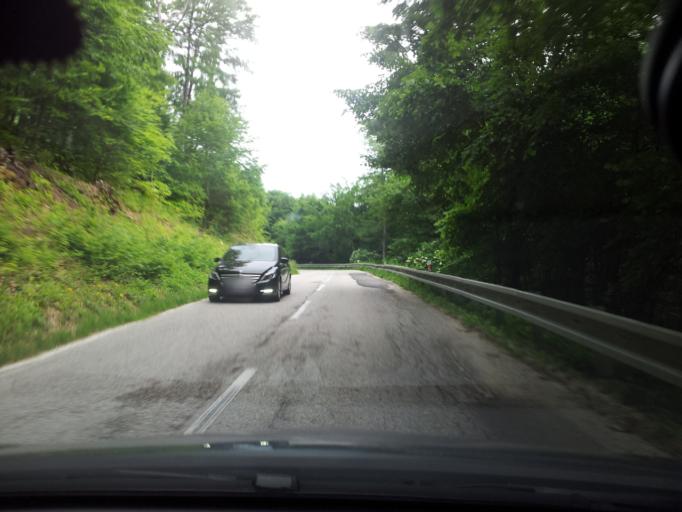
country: SK
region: Nitriansky
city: Partizanske
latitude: 48.5696
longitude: 18.4569
